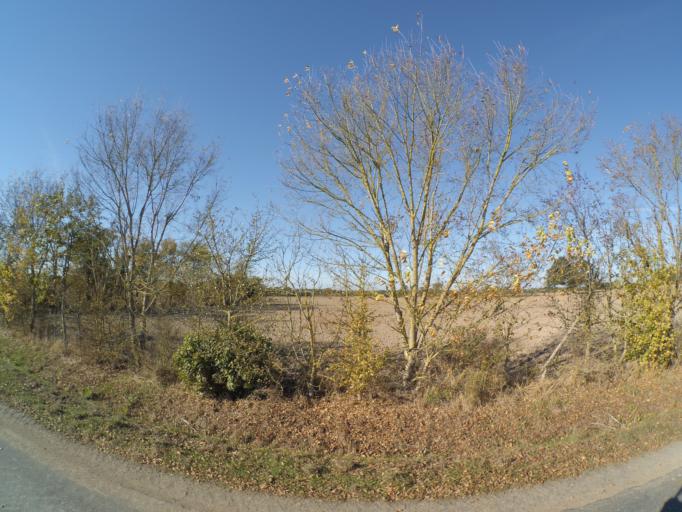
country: FR
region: Pays de la Loire
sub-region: Departement de la Loire-Atlantique
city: Saint-Lumine-de-Clisson
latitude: 47.0701
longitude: -1.3336
